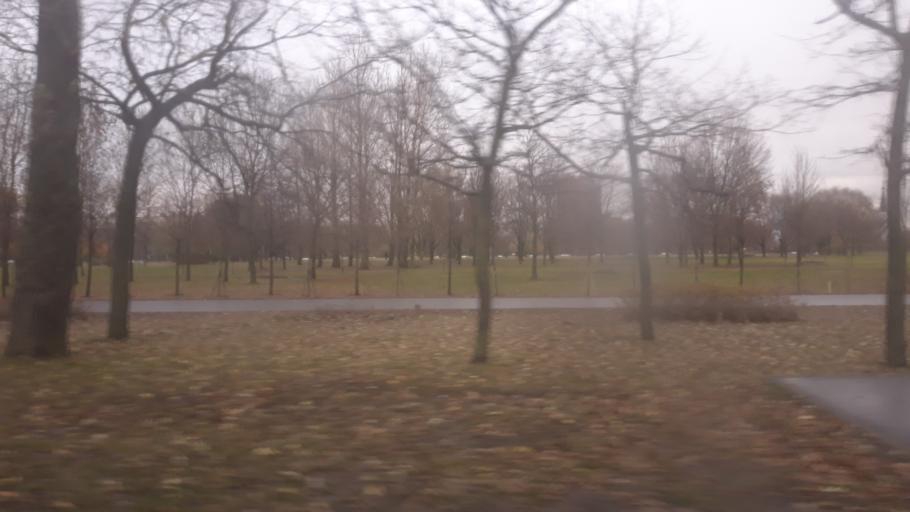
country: RU
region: St.-Petersburg
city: Kupchino
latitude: 59.8383
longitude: 30.3226
